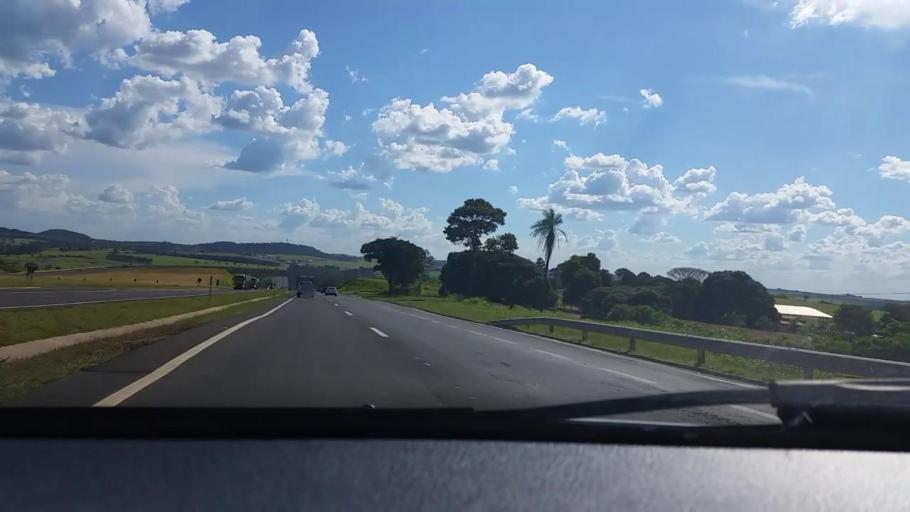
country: BR
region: Sao Paulo
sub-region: Bauru
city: Bauru
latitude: -22.3963
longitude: -49.0854
